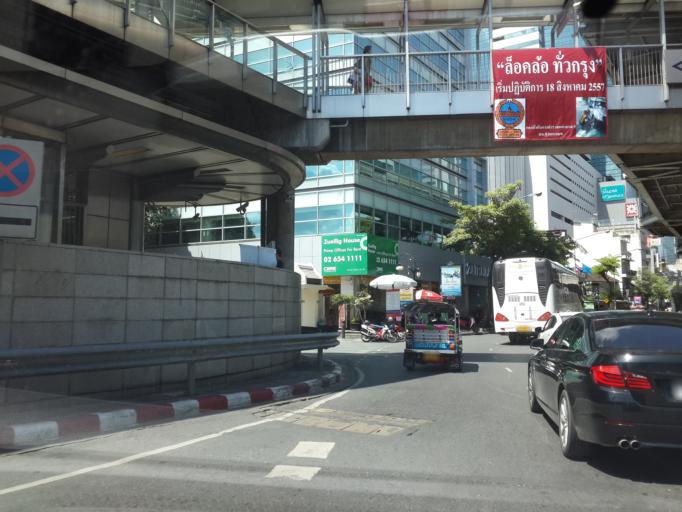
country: TH
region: Bangkok
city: Bang Rak
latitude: 13.7294
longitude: 100.5364
